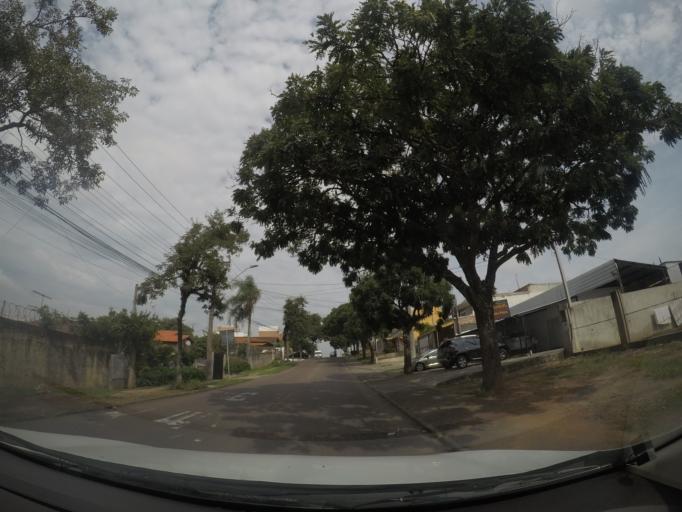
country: BR
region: Parana
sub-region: Sao Jose Dos Pinhais
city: Sao Jose dos Pinhais
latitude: -25.5185
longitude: -49.2773
